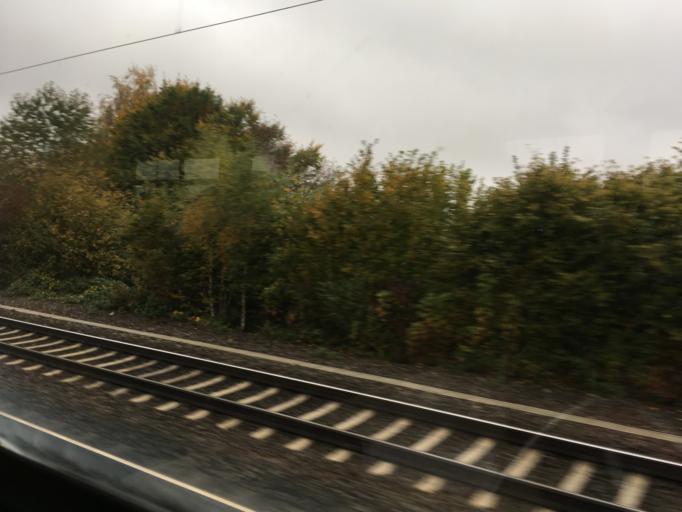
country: DE
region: Lower Saxony
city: Osnabrueck
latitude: 52.2596
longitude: 8.0265
